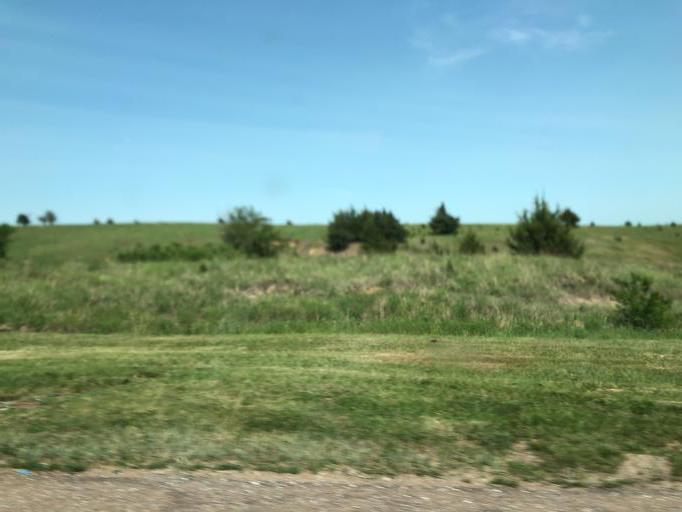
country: US
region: Nebraska
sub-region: Thayer County
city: Hebron
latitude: 40.1715
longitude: -97.5740
